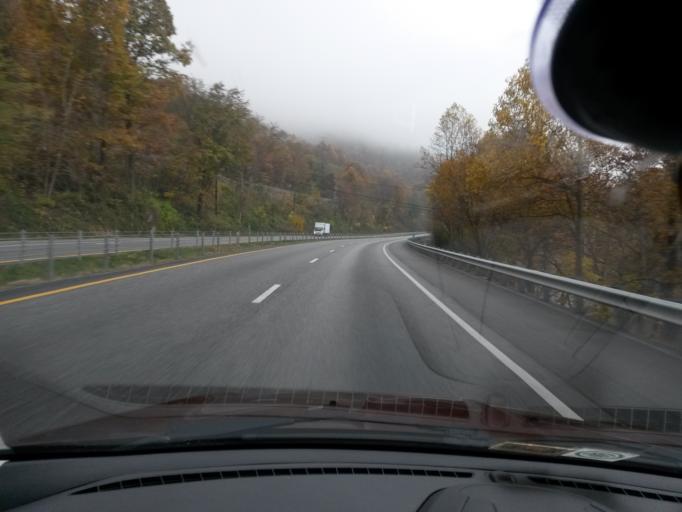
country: US
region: Virginia
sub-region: City of Covington
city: Fairlawn
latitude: 37.7805
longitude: -79.9099
